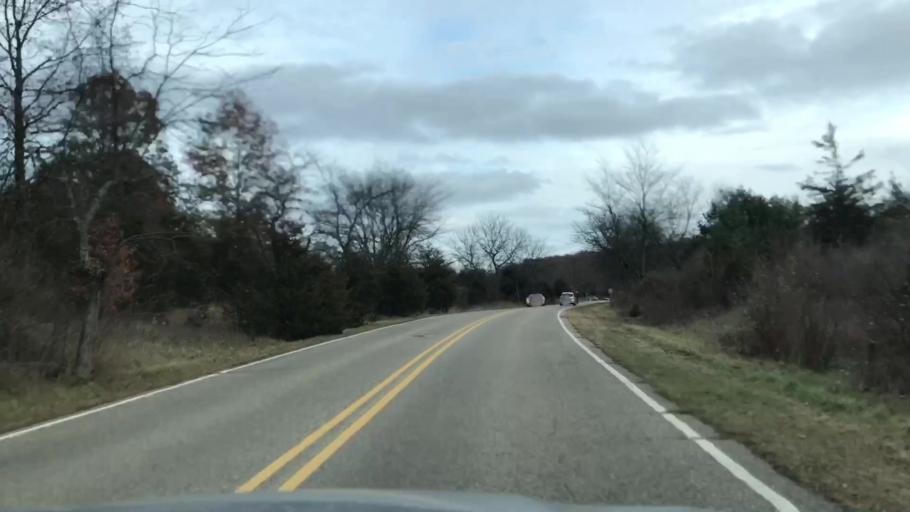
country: US
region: Michigan
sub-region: Oakland County
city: South Lyon
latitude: 42.5115
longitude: -83.6796
